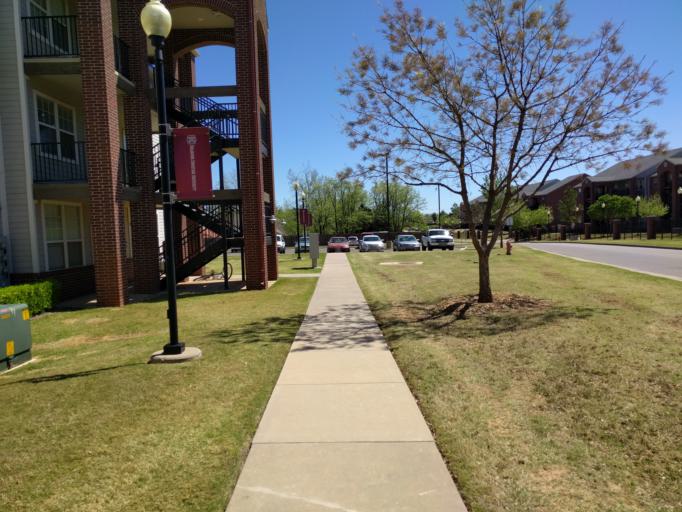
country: US
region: Oklahoma
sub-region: Oklahoma County
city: Edmond
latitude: 35.6110
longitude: -97.4635
